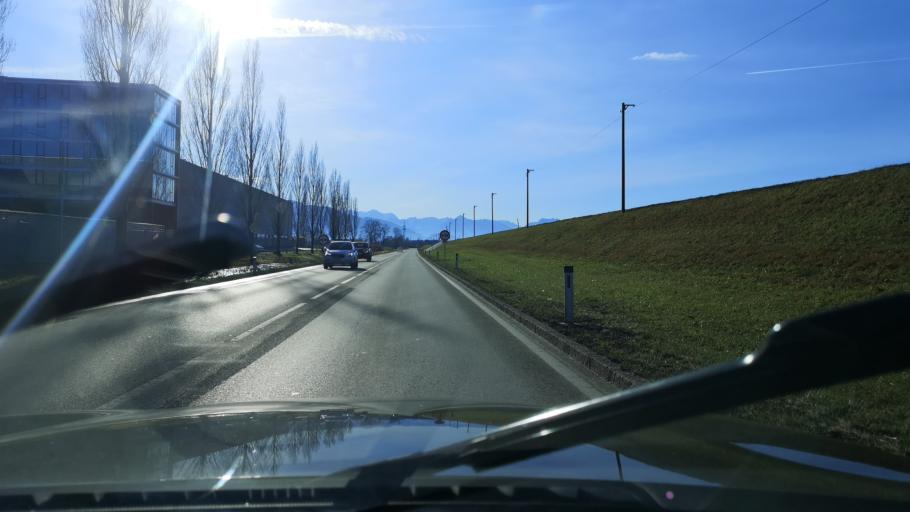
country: AT
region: Vorarlberg
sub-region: Politischer Bezirk Bregenz
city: Fussach
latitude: 47.4686
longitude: 9.6710
